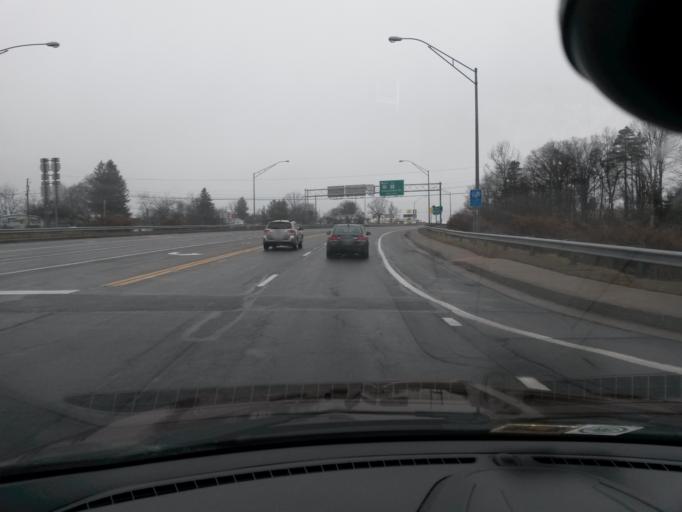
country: US
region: West Virginia
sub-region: Raleigh County
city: Beaver
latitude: 37.7702
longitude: -81.1595
